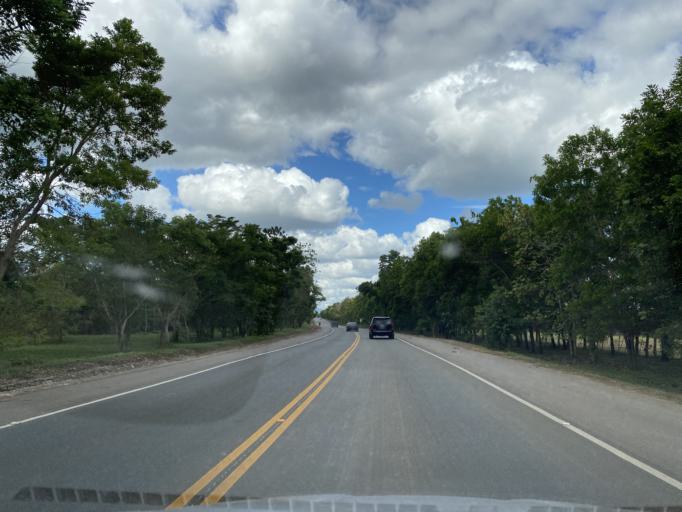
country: DO
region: Santo Domingo
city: Guerra
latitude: 18.6690
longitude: -69.7424
